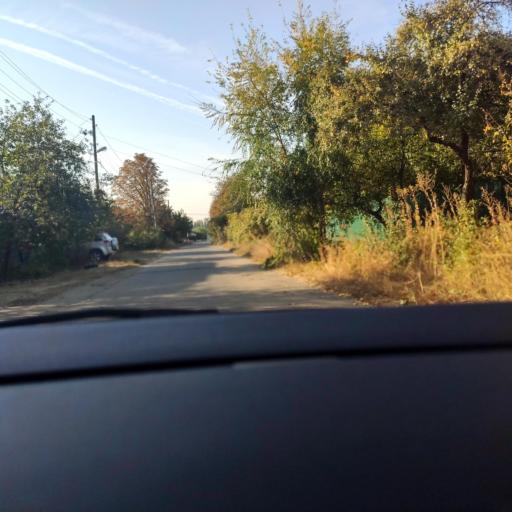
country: RU
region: Voronezj
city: Voronezh
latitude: 51.6299
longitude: 39.1691
